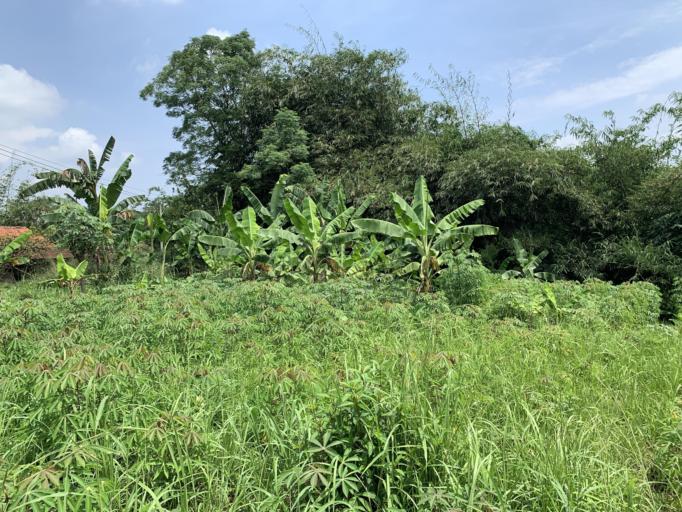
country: ID
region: West Java
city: Serpong
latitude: -6.3931
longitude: 106.6223
